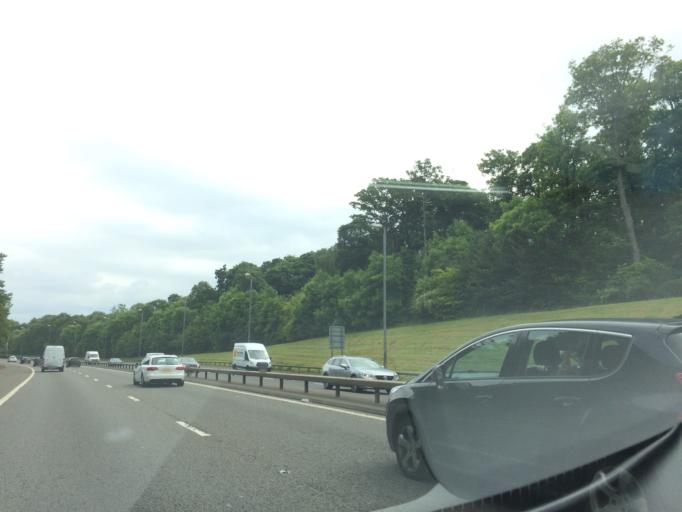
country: GB
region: Scotland
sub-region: East Renfrewshire
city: Giffnock
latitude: 55.8350
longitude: -4.3251
